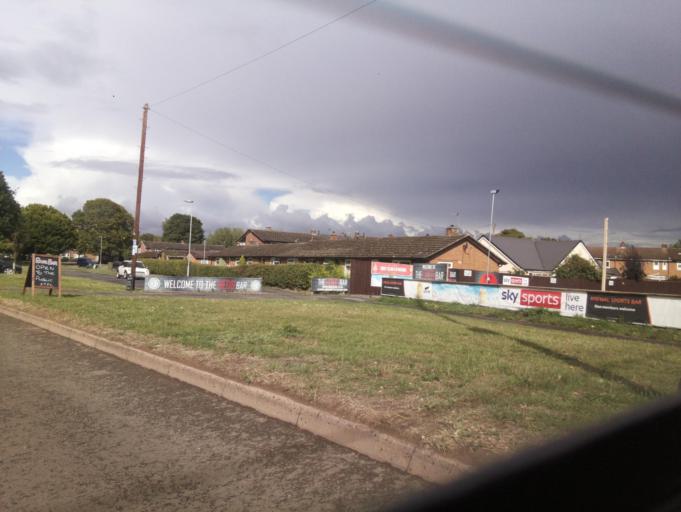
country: GB
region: England
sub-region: Shropshire
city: Shifnal
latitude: 52.6743
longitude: -2.3713
